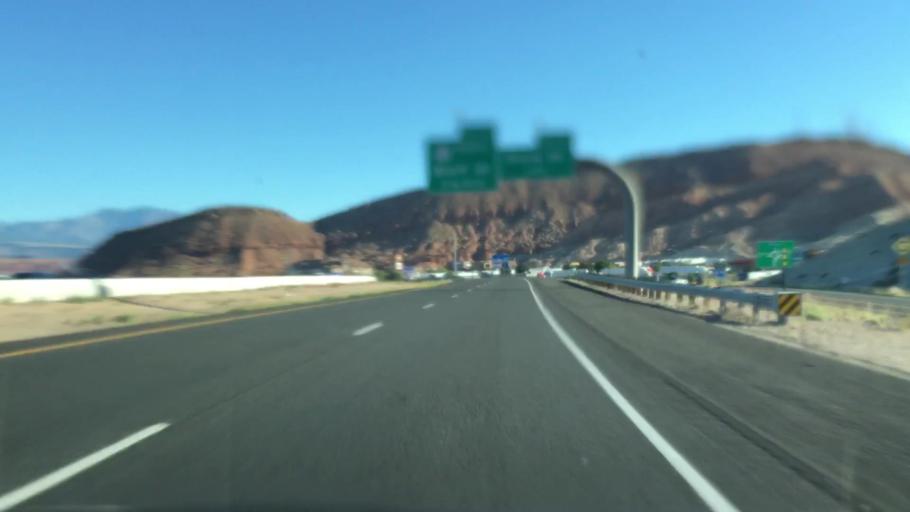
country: US
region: Utah
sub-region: Washington County
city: Saint George
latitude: 37.0570
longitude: -113.5857
